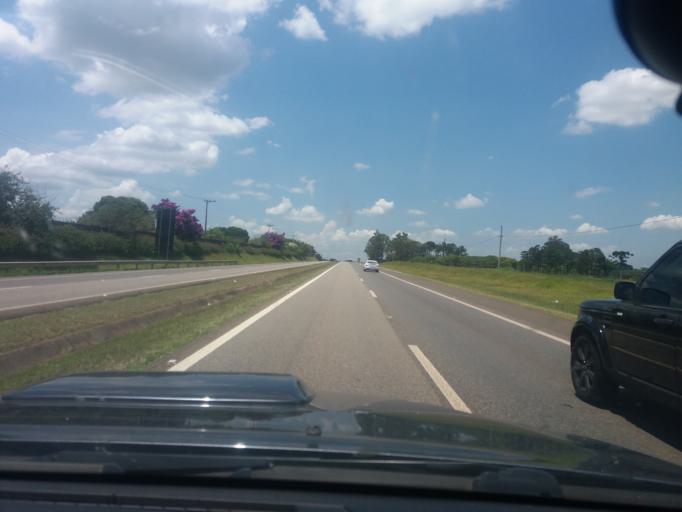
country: BR
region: Sao Paulo
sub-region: Itapetininga
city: Itapetininga
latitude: -23.5831
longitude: -47.9828
